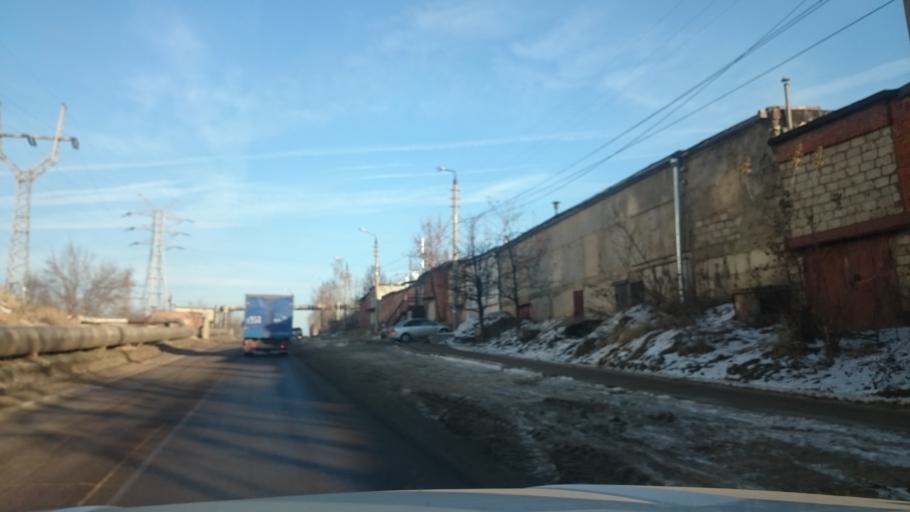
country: RU
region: Tula
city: Tula
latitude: 54.2139
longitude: 37.6857
